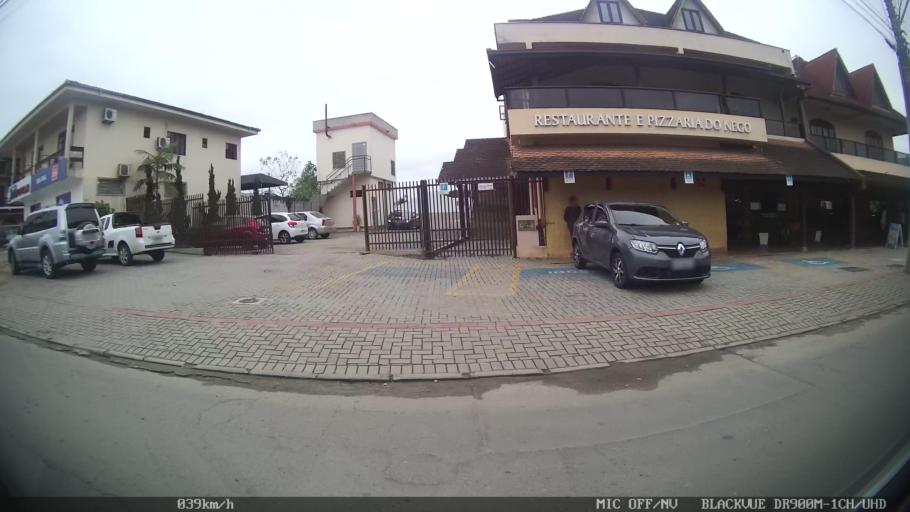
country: BR
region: Santa Catarina
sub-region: Joinville
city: Joinville
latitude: -26.3351
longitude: -48.8168
